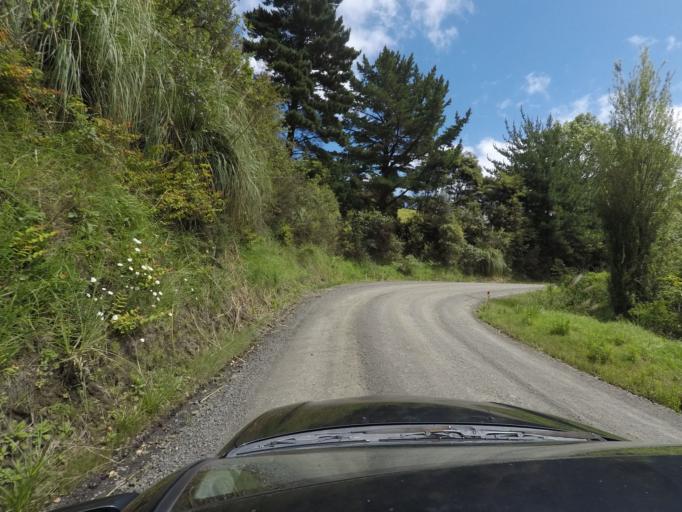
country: NZ
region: Auckland
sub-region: Auckland
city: Warkworth
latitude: -36.4883
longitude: 174.6140
